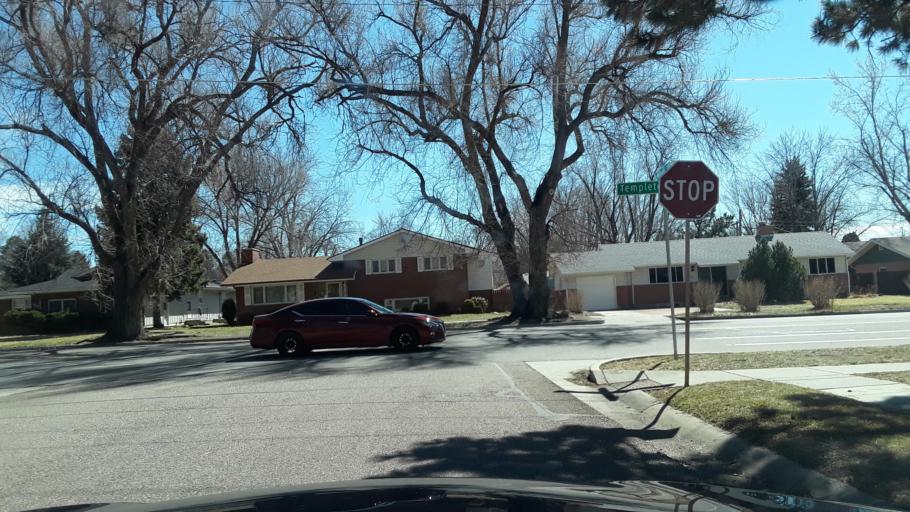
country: US
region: Colorado
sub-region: El Paso County
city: Colorado Springs
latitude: 38.8696
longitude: -104.8043
